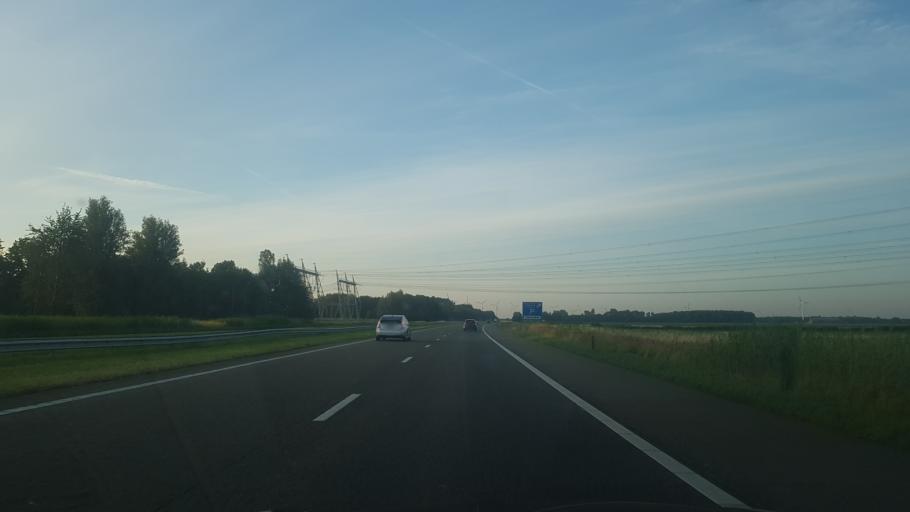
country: NL
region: Flevoland
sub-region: Gemeente Lelystad
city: Lelystad
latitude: 52.5726
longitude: 5.5377
